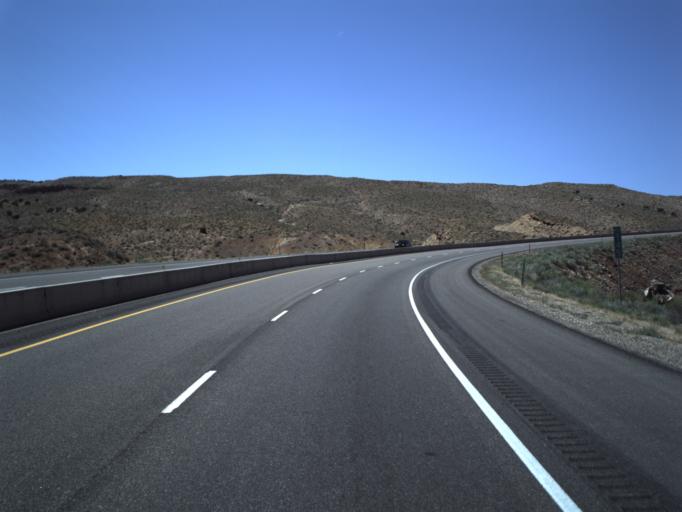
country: US
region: Utah
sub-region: Carbon County
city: East Carbon City
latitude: 38.9243
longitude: -110.4502
